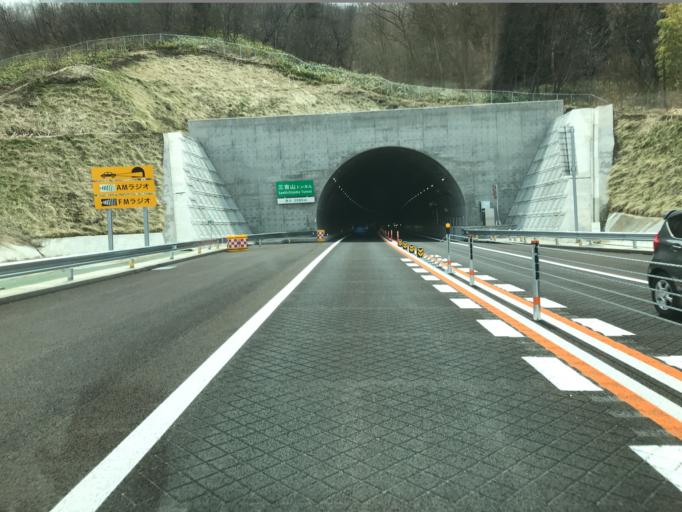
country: JP
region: Yamagata
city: Kaminoyama
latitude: 38.1600
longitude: 140.3076
